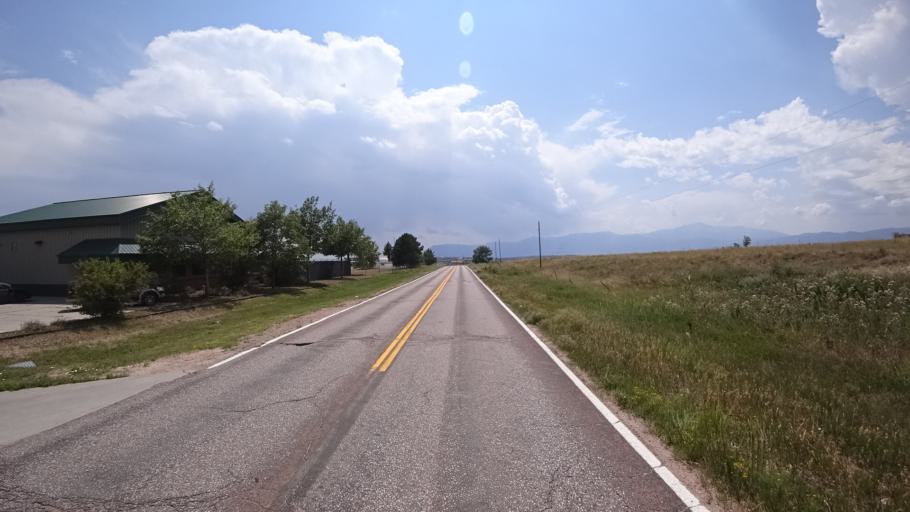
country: US
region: Colorado
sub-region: El Paso County
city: Black Forest
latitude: 38.9378
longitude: -104.7077
